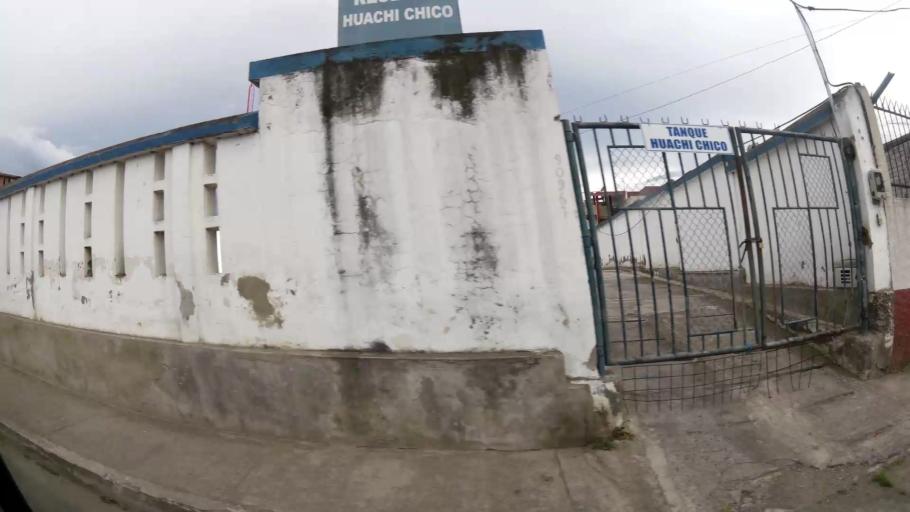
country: EC
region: Tungurahua
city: Ambato
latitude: -1.2740
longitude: -78.6353
